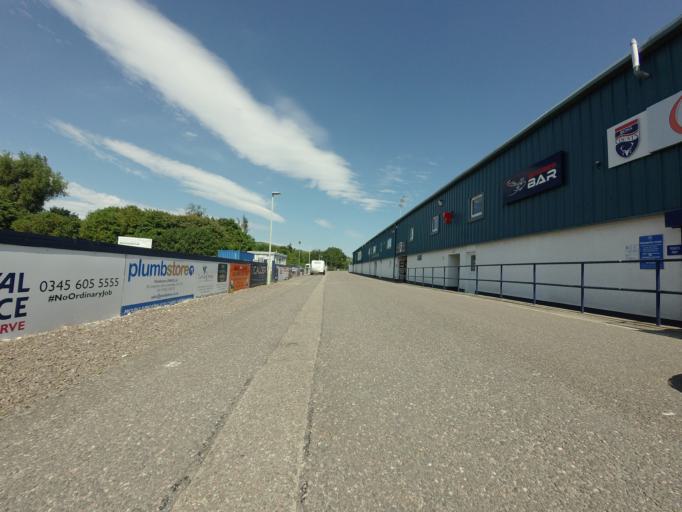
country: GB
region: Scotland
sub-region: Highland
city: Dingwall
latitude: 57.5956
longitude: -4.4202
